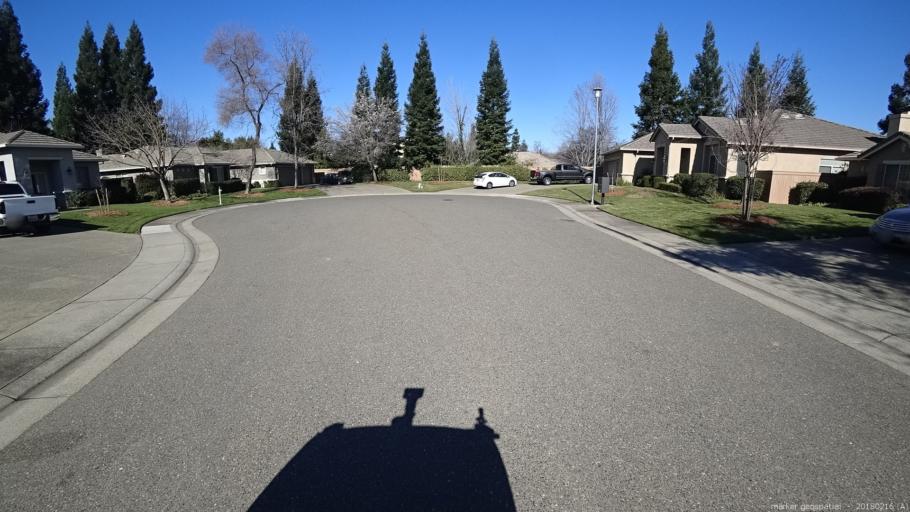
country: US
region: California
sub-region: Sacramento County
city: Gold River
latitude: 38.6216
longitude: -121.2412
